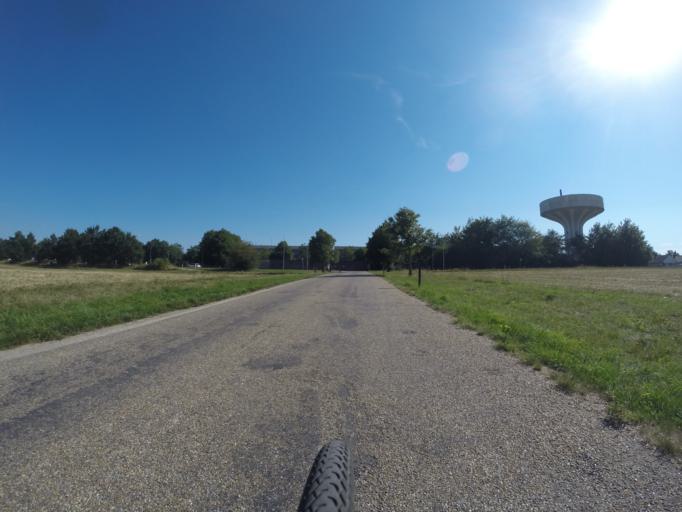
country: DK
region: Capital Region
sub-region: Herlev Kommune
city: Herlev
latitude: 55.7456
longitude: 12.4326
